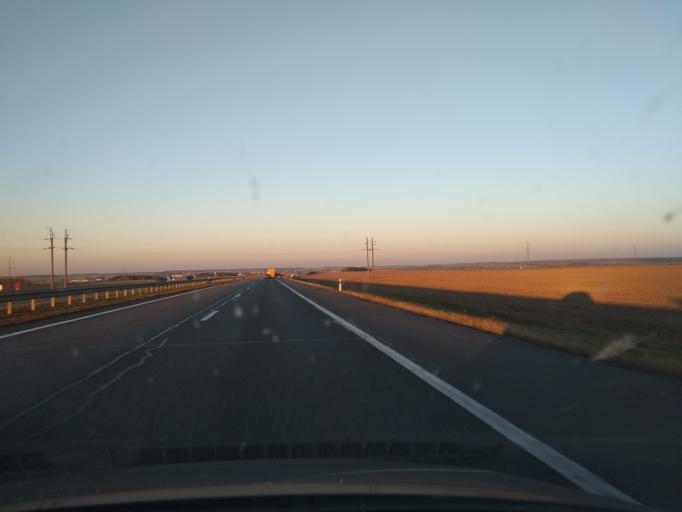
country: BY
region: Minsk
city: Snow
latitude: 53.3231
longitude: 26.4105
